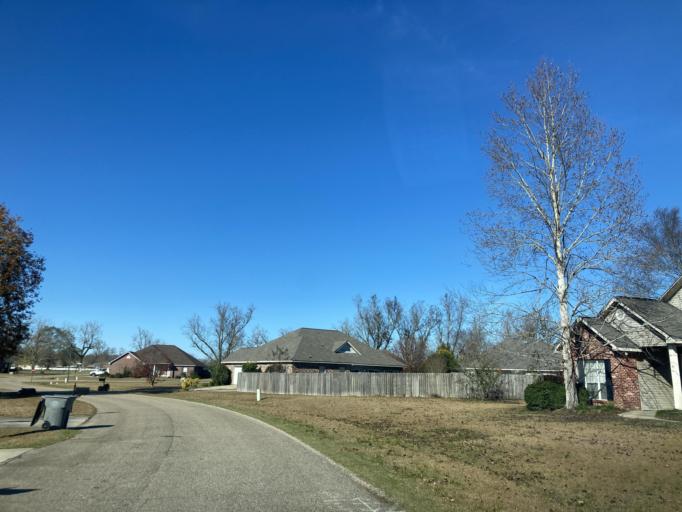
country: US
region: Mississippi
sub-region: Forrest County
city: Petal
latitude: 31.3191
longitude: -89.1855
